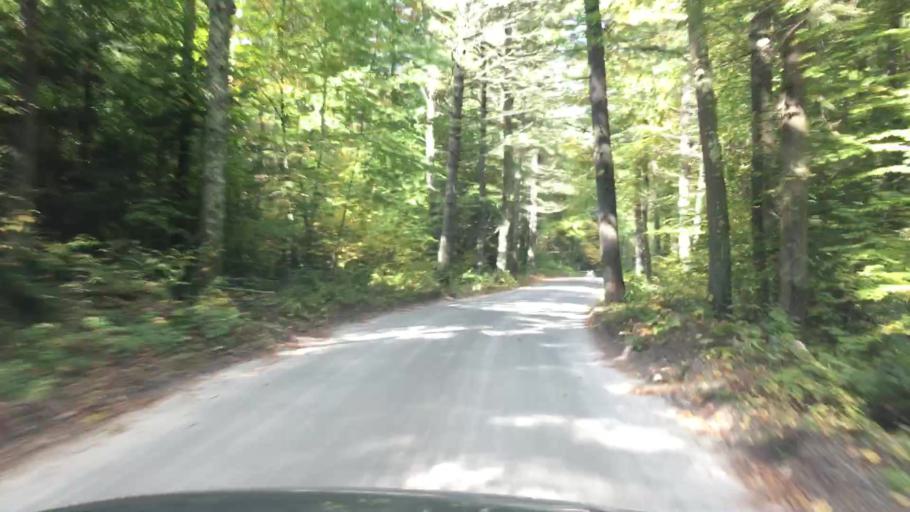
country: US
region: Connecticut
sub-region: Tolland County
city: Stafford
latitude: 41.9879
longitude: -72.3307
